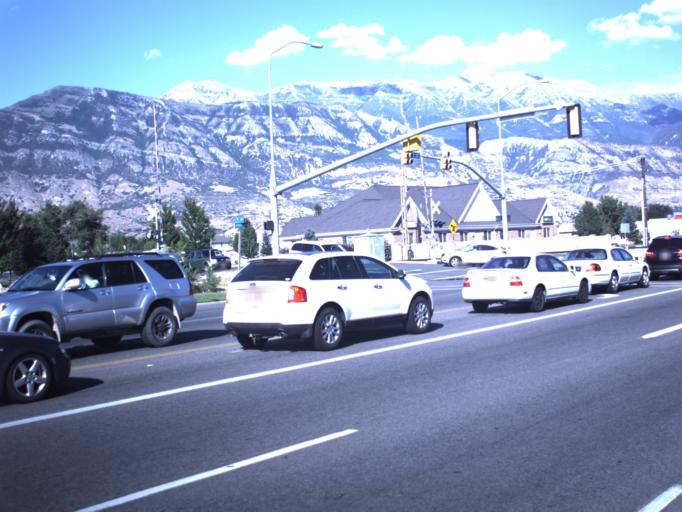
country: US
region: Utah
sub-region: Utah County
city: American Fork
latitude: 40.3729
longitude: -111.7813
